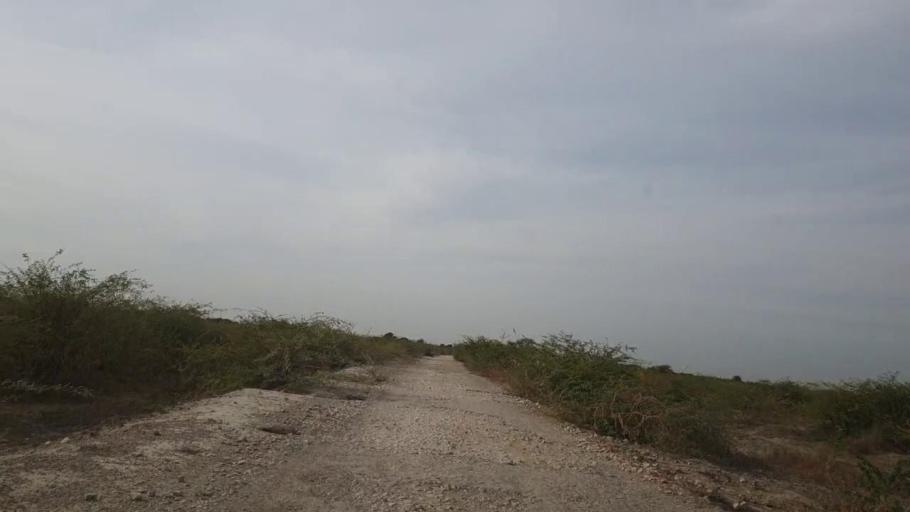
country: PK
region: Sindh
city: Nabisar
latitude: 24.9978
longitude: 69.5444
